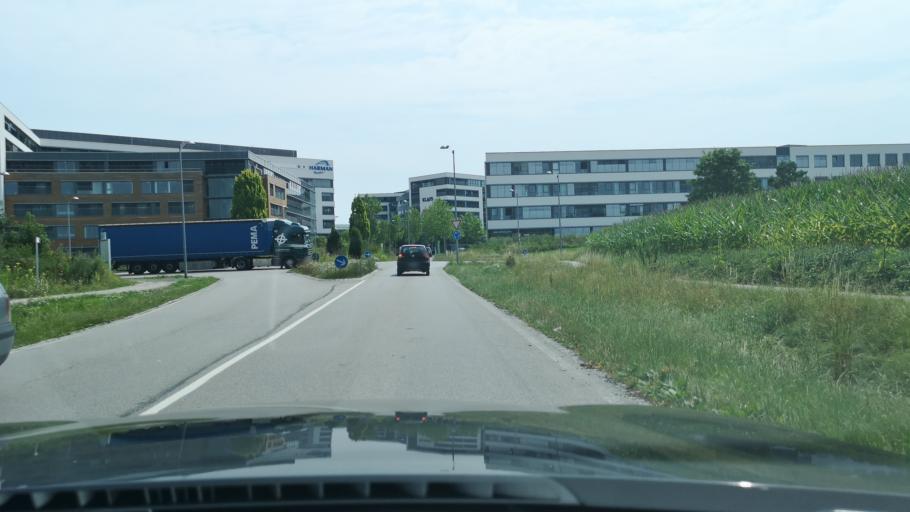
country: DE
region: Bavaria
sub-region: Upper Bavaria
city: Garching bei Munchen
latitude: 48.2524
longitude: 11.6305
